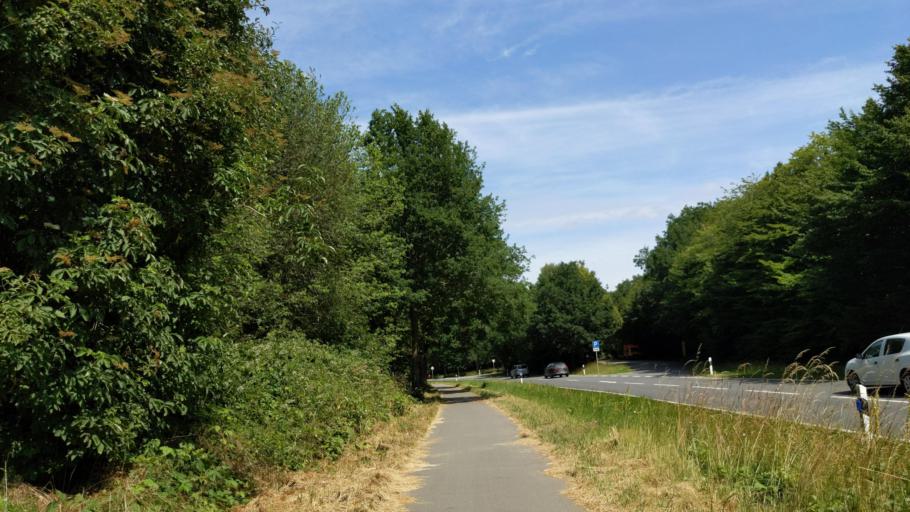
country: DE
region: Schleswig-Holstein
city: Malente
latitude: 54.1502
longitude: 10.5350
